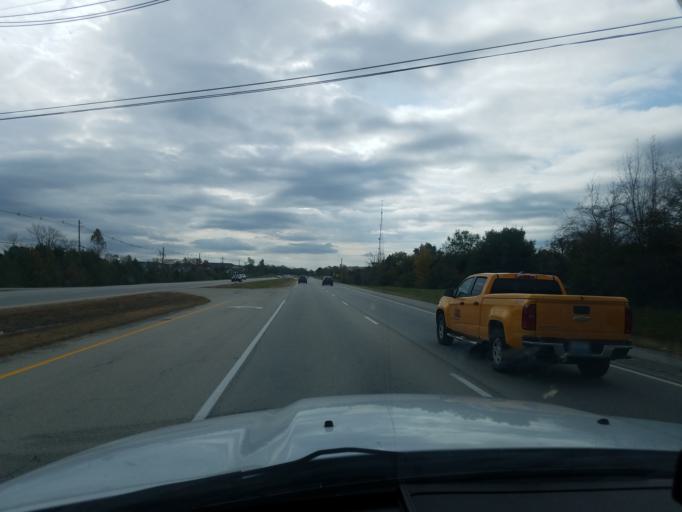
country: US
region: Kentucky
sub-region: Jefferson County
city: Fern Creek
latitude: 38.1102
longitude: -85.5679
